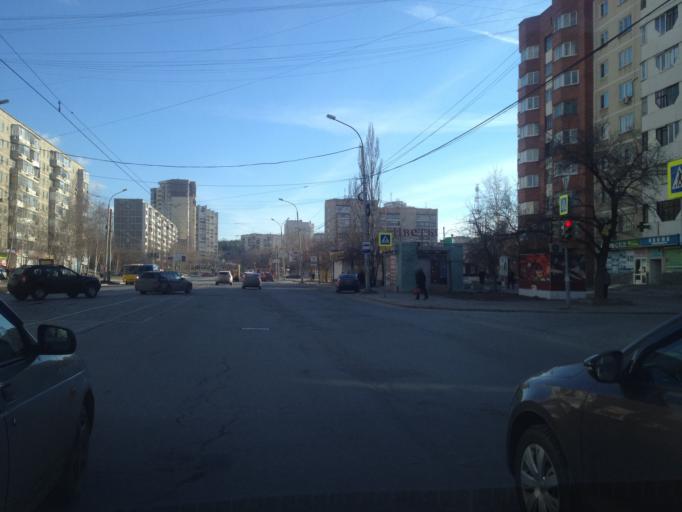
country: RU
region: Sverdlovsk
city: Yekaterinburg
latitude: 56.8210
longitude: 60.5687
